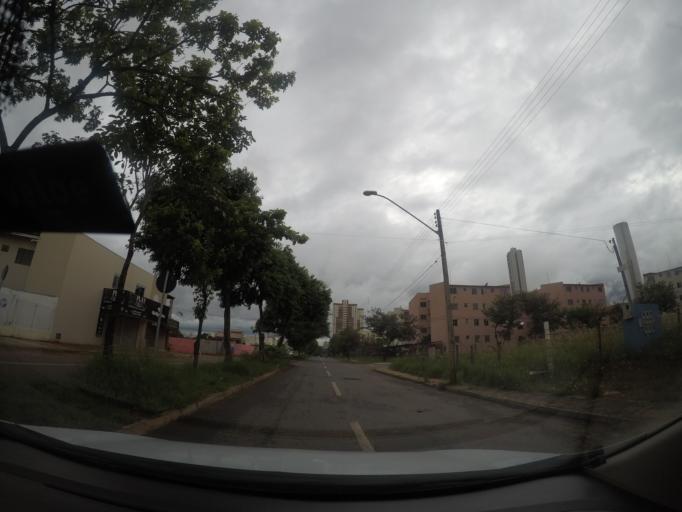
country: BR
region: Goias
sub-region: Goiania
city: Goiania
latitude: -16.7331
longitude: -49.2874
